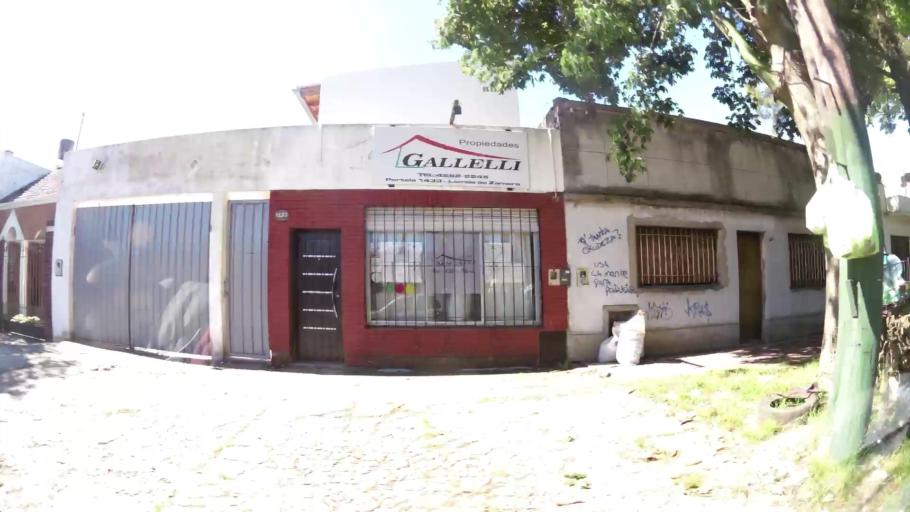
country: AR
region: Buenos Aires
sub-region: Partido de Lomas de Zamora
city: Lomas de Zamora
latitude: -34.7547
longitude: -58.4168
